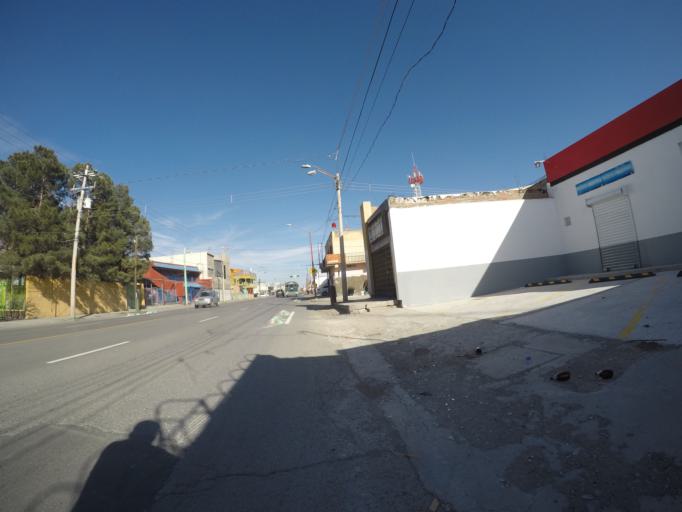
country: MX
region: Chihuahua
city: Ciudad Juarez
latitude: 31.7321
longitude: -106.4556
